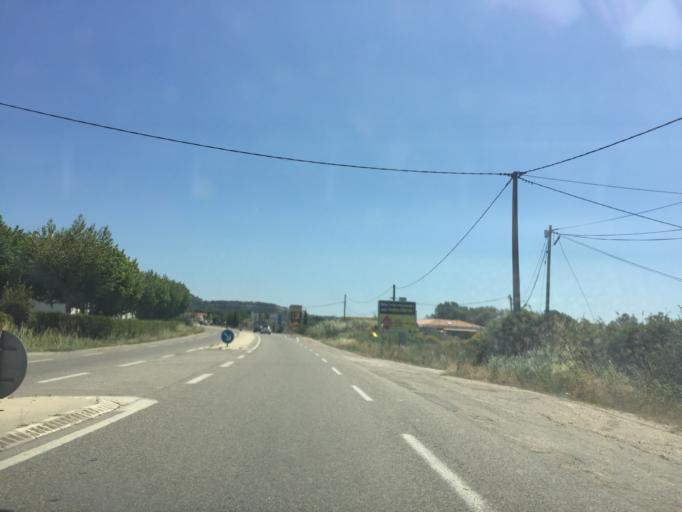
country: FR
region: Provence-Alpes-Cote d'Azur
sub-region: Departement des Bouches-du-Rhone
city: Rognac
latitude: 43.4881
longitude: 5.2202
